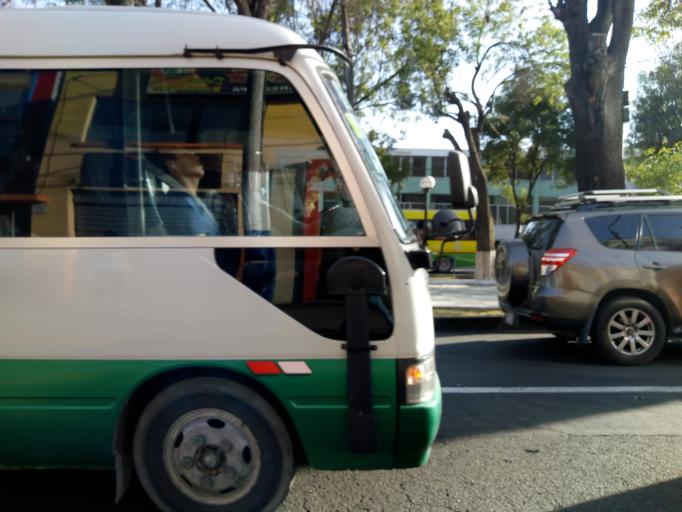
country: PE
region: Arequipa
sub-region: Provincia de Arequipa
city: Arequipa
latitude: -16.3911
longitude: -71.5432
